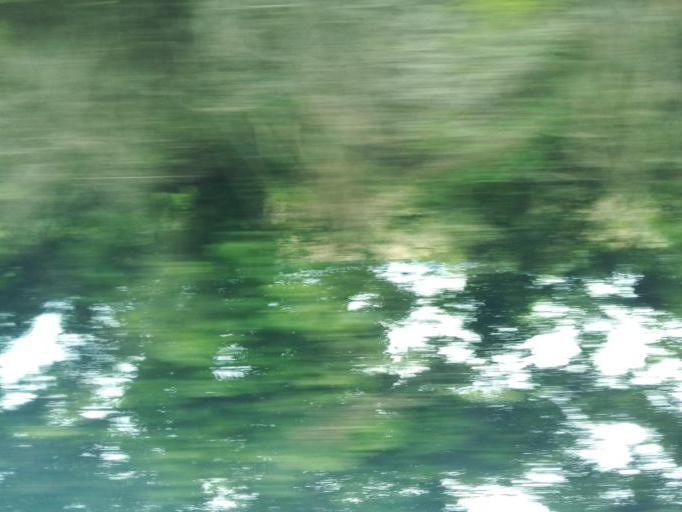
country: BR
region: Minas Gerais
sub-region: Ipatinga
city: Ipatinga
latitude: -19.4652
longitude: -42.4762
